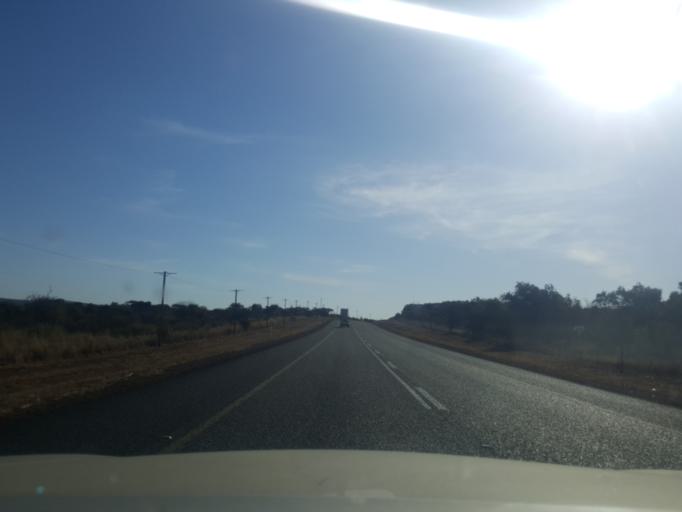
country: ZA
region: North-West
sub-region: Ngaka Modiri Molema District Municipality
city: Zeerust
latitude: -25.5374
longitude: 26.0328
